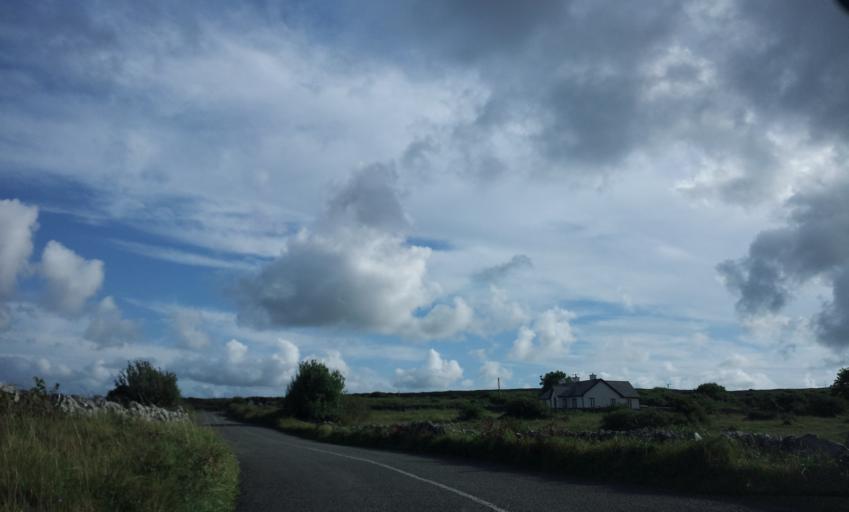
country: IE
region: Connaught
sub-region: County Galway
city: Bearna
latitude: 53.0715
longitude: -9.1556
